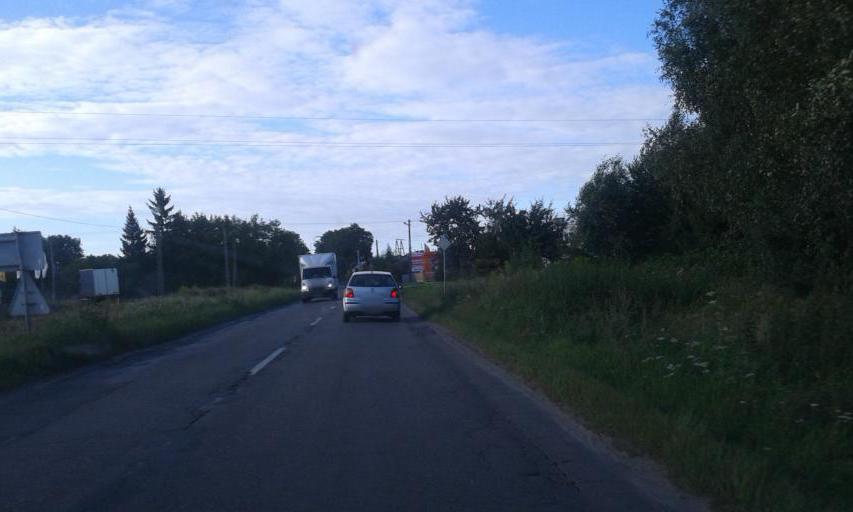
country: PL
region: West Pomeranian Voivodeship
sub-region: Koszalin
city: Koszalin
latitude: 54.1646
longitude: 16.1848
